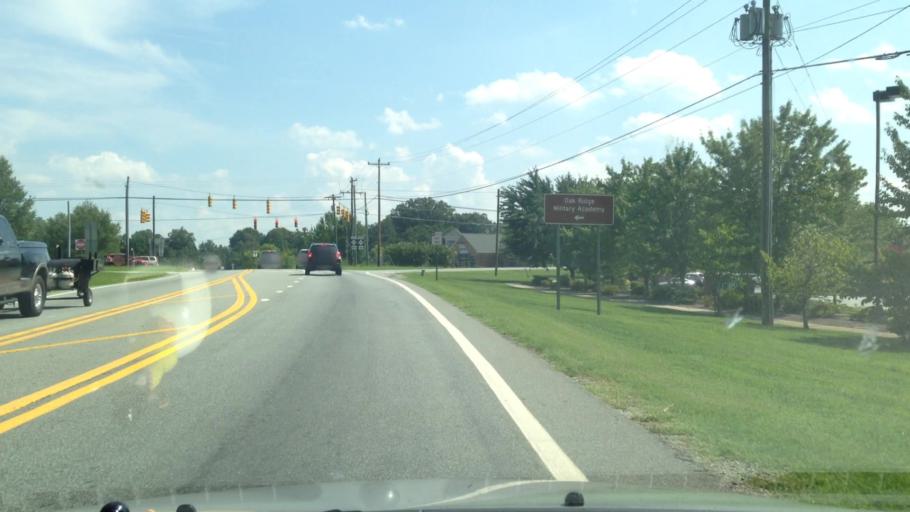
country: US
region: North Carolina
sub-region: Guilford County
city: Oak Ridge
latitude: 36.1746
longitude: -79.9894
